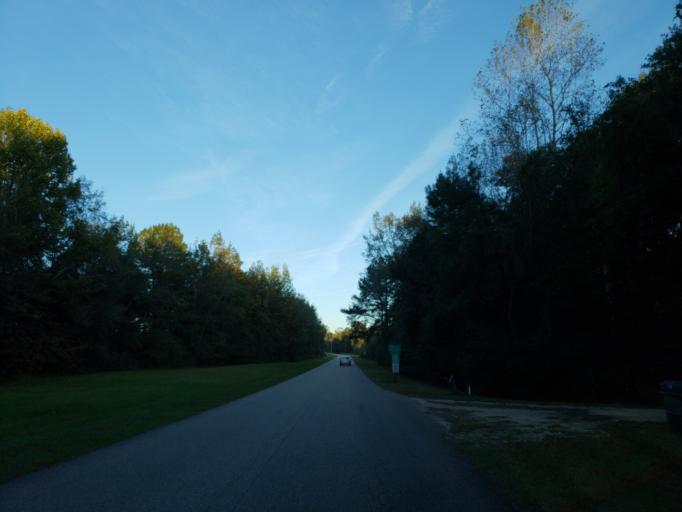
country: US
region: Mississippi
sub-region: Wayne County
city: Belmont
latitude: 31.4364
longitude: -88.4891
